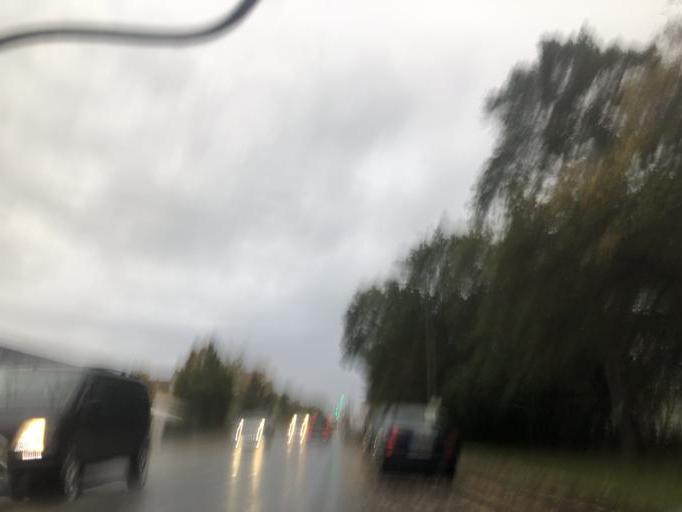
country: DE
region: Bavaria
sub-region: Regierungsbezirk Mittelfranken
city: Furth
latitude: 49.5072
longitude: 10.9776
